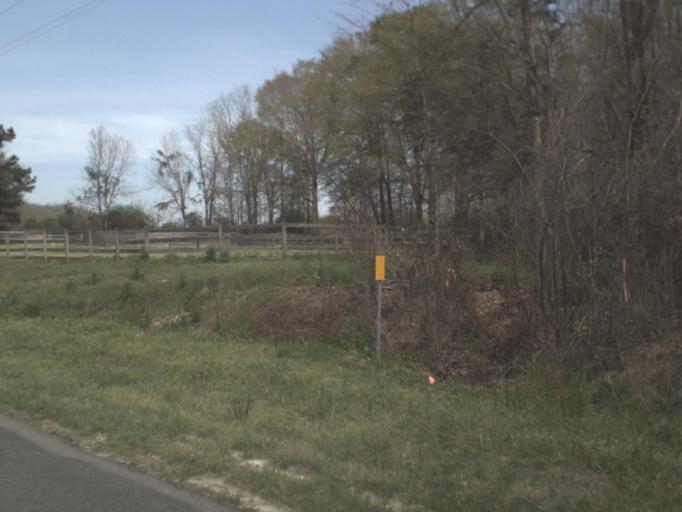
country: US
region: Alabama
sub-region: Geneva County
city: Geneva
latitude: 30.9143
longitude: -85.9595
